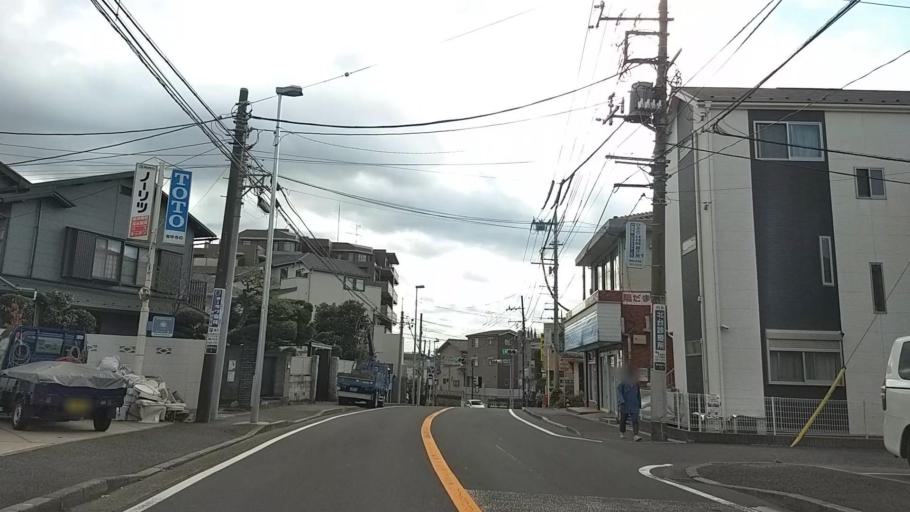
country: JP
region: Kanagawa
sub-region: Kawasaki-shi
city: Kawasaki
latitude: 35.5106
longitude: 139.6641
